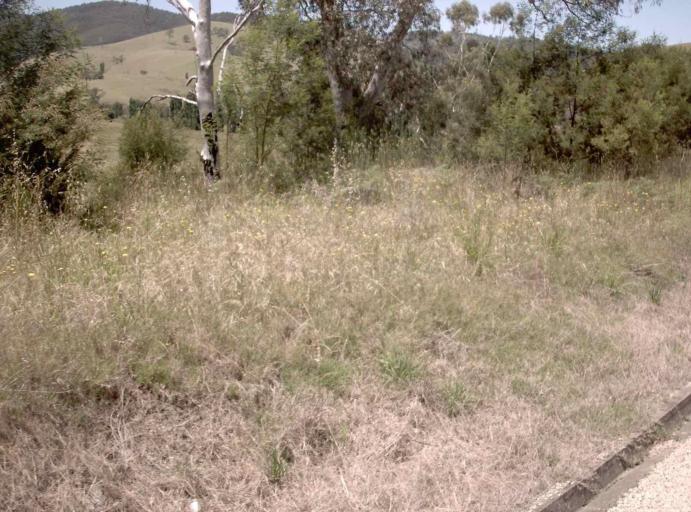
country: AU
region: Victoria
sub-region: East Gippsland
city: Bairnsdale
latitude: -37.5071
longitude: 147.8403
